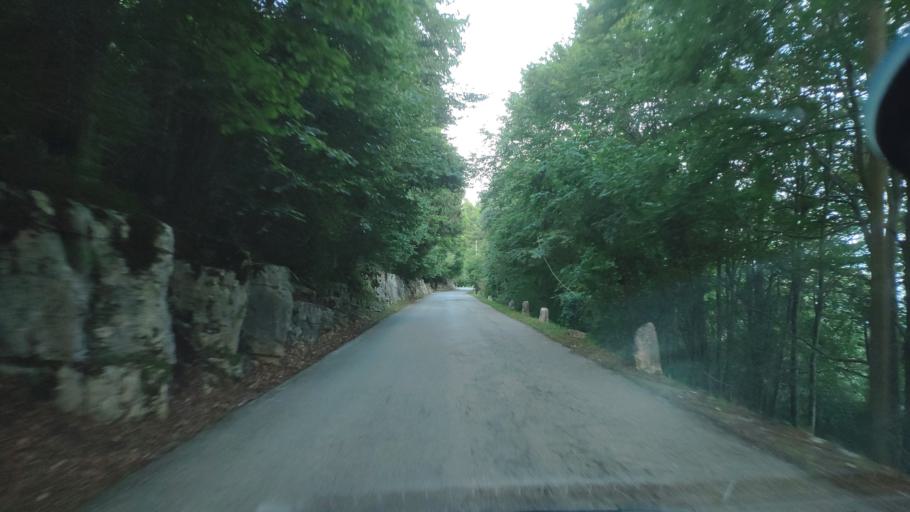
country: IT
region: Veneto
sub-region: Provincia di Vicenza
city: Calvene
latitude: 45.7917
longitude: 11.5089
